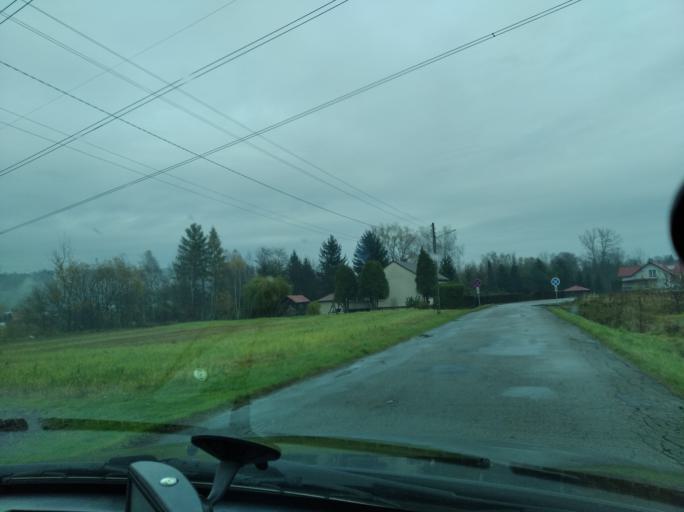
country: PL
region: Subcarpathian Voivodeship
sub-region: Powiat strzyzowski
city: Babica
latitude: 49.9272
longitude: 21.8692
